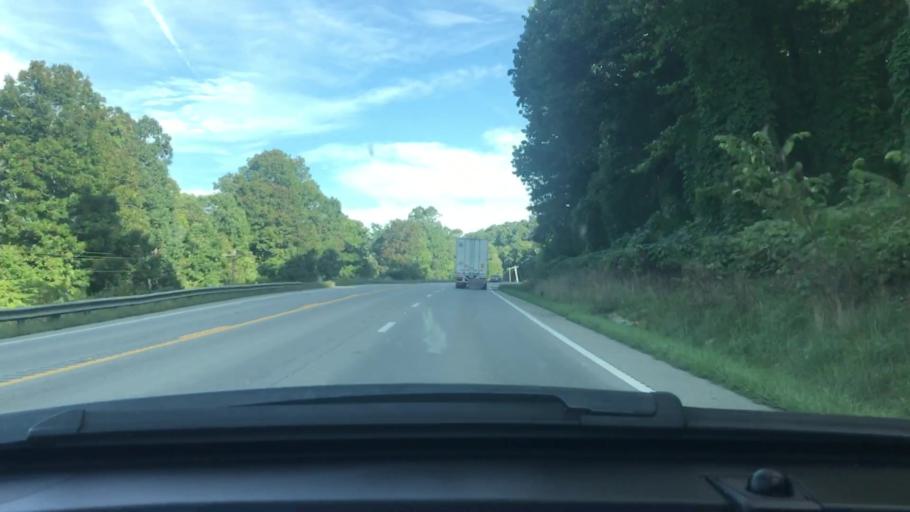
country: US
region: Arkansas
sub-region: Sharp County
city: Cherokee Village
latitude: 36.3027
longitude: -91.4138
